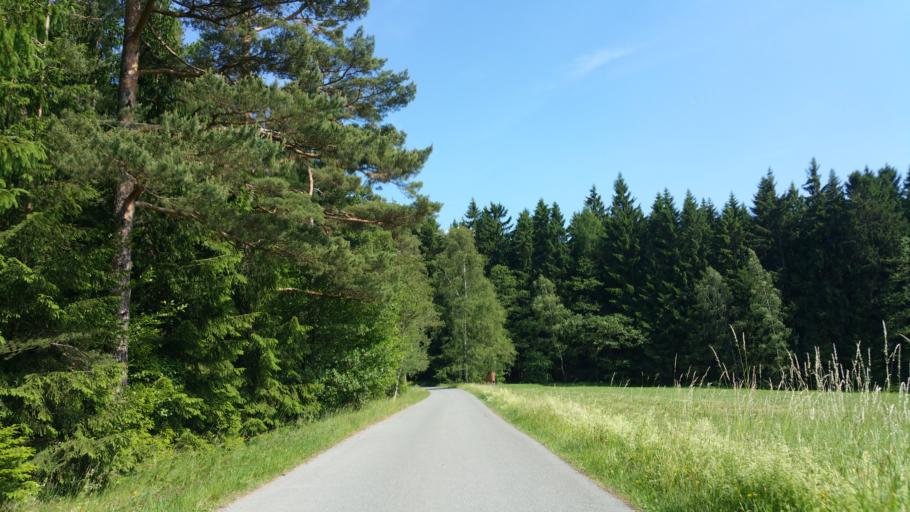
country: DE
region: Bavaria
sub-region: Upper Franconia
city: Schwarzenbach an der Saale
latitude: 50.1994
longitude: 11.9903
